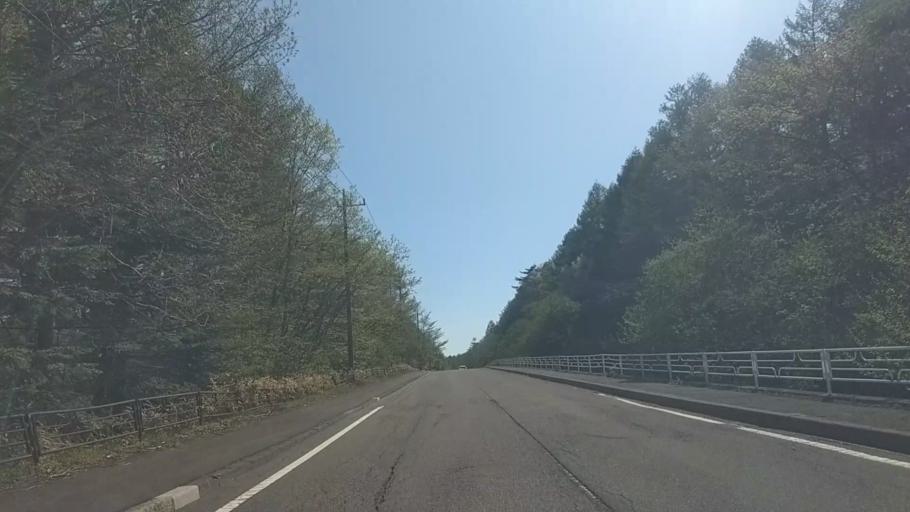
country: JP
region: Yamanashi
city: Nirasaki
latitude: 35.9379
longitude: 138.4306
